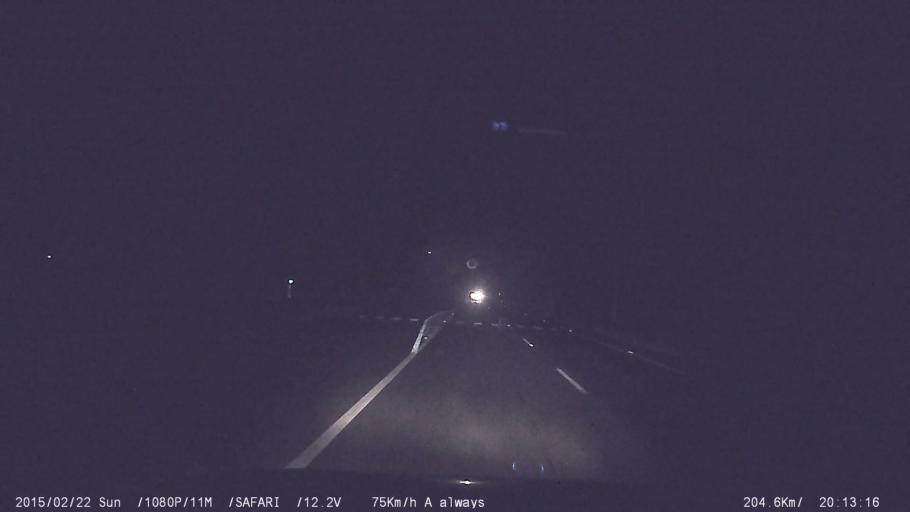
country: IN
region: Tamil Nadu
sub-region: Dindigul
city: Nilakottai
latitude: 10.2452
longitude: 77.8247
